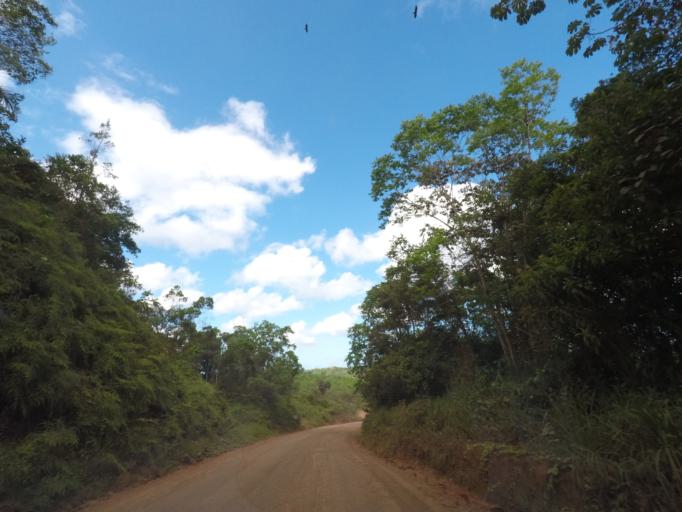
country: BR
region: Bahia
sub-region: Itacare
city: Itacare
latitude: -14.2199
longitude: -39.0900
